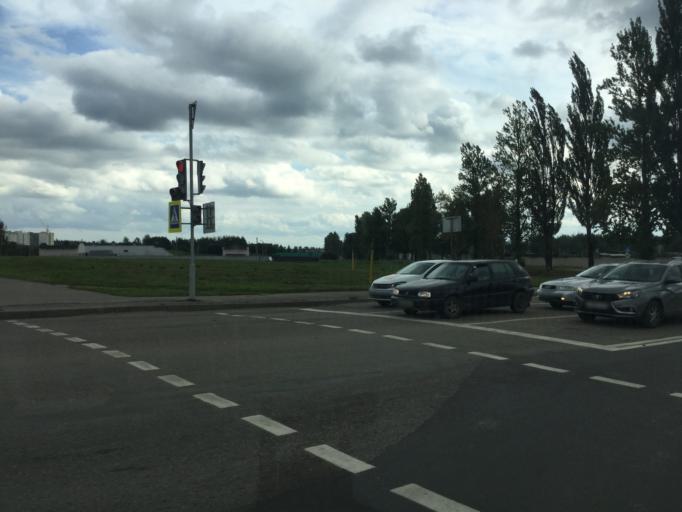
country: BY
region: Vitebsk
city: Vitebsk
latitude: 55.1664
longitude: 30.2535
